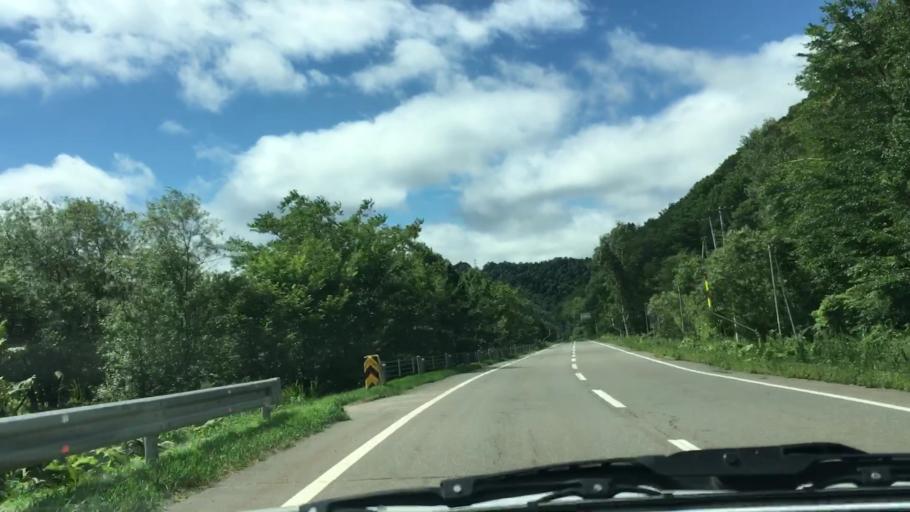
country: JP
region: Hokkaido
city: Kitami
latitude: 43.3620
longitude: 143.8530
